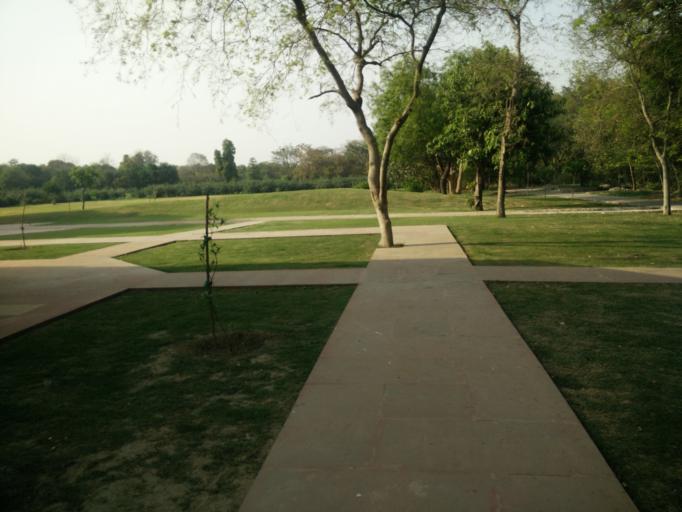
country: IN
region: NCT
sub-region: New Delhi
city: New Delhi
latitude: 28.5962
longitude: 77.2468
